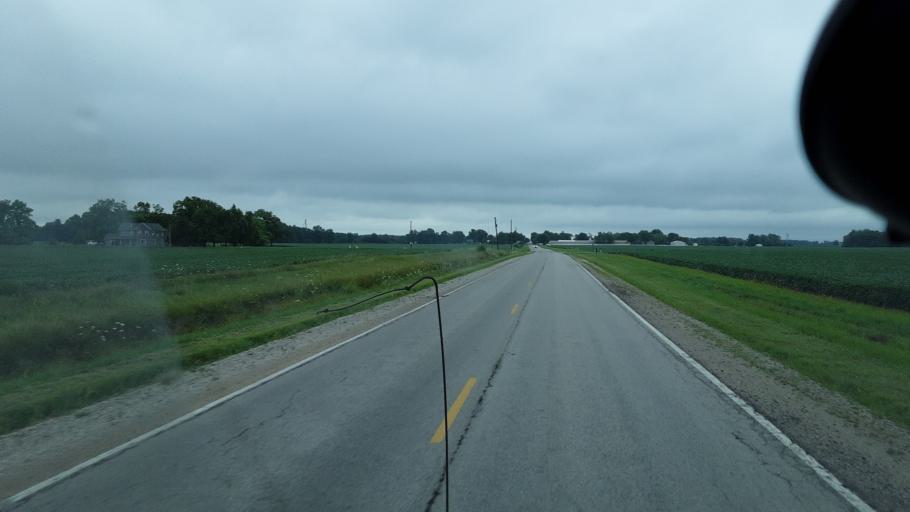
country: US
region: Indiana
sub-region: Wells County
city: Bluffton
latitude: 40.7882
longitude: -85.0909
